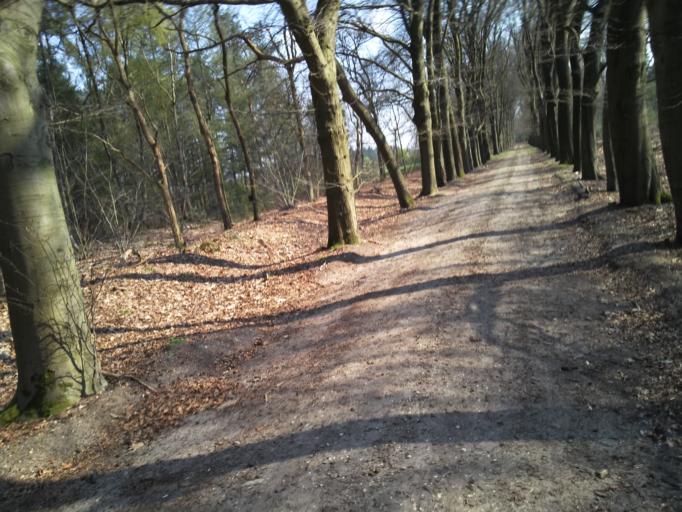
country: NL
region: Gelderland
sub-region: Gemeente Renkum
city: Oosterbeek
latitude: 52.0300
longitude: 5.8314
